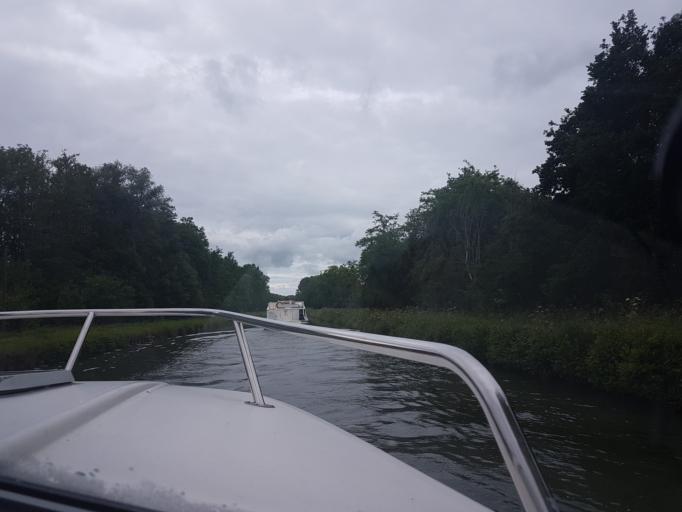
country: FR
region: Bourgogne
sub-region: Departement de l'Yonne
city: Vermenton
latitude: 47.6532
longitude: 3.6708
